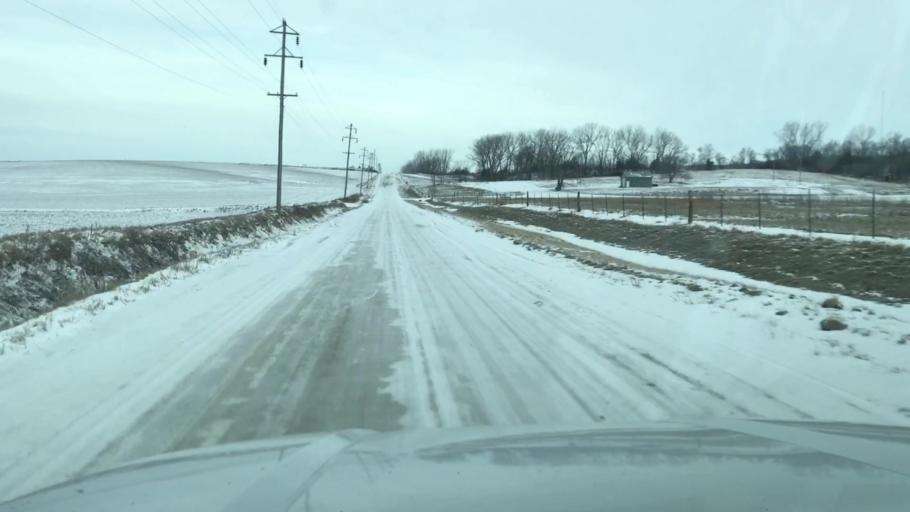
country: US
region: Missouri
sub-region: Holt County
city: Oregon
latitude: 40.1301
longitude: -95.0543
